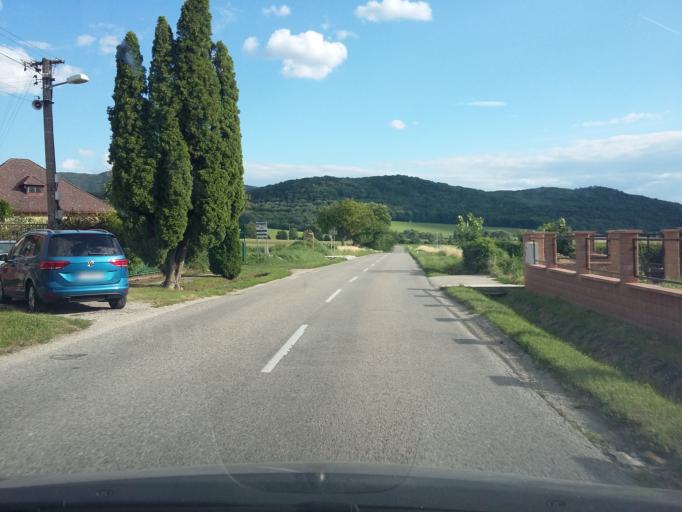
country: SK
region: Trnavsky
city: Smolenice
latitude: 48.5523
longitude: 17.3498
